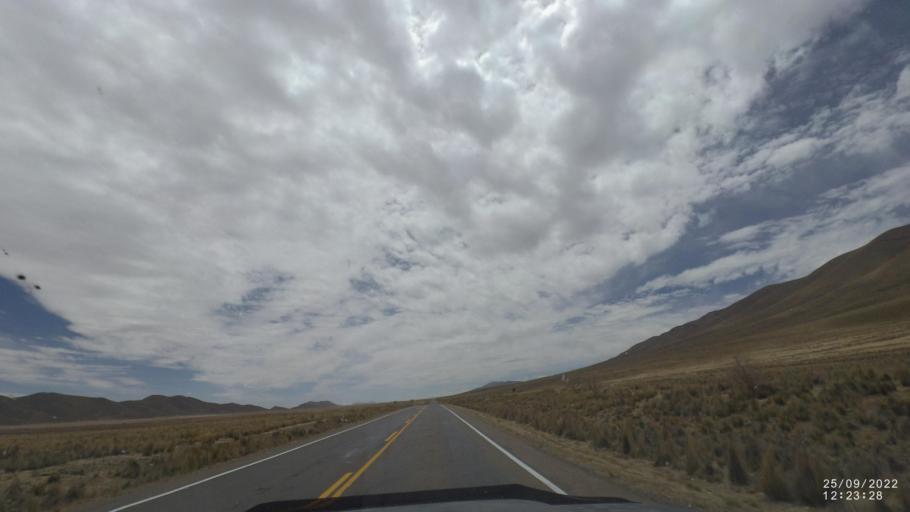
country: BO
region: Oruro
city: Poopo
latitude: -18.3721
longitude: -66.9805
